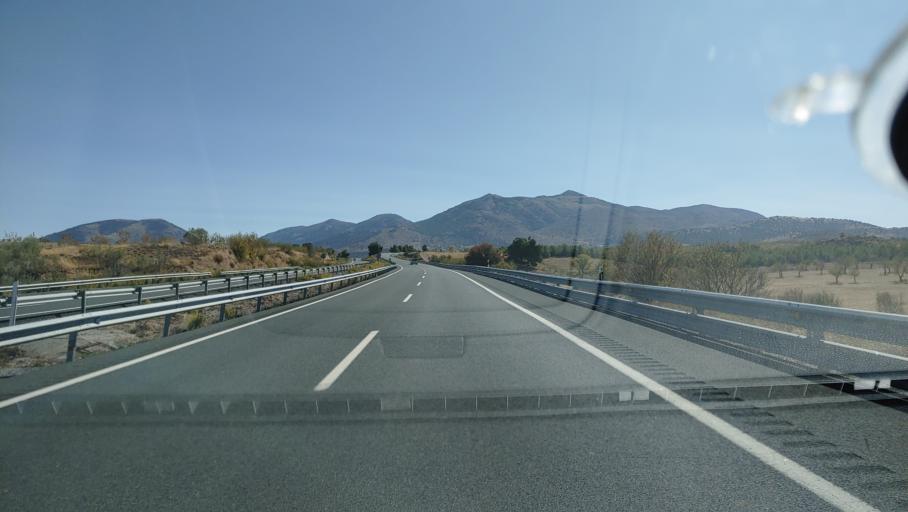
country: ES
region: Andalusia
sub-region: Provincia de Granada
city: Gor
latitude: 37.3950
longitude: -2.9749
